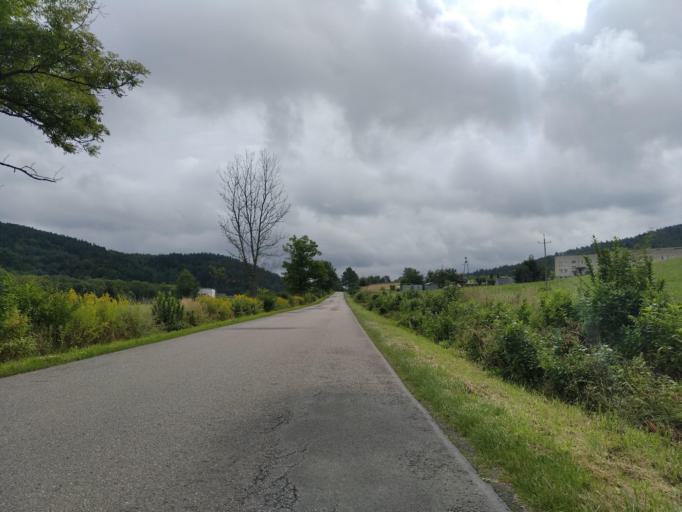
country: PL
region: Subcarpathian Voivodeship
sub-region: Powiat brzozowski
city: Nozdrzec
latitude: 49.7448
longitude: 22.2352
